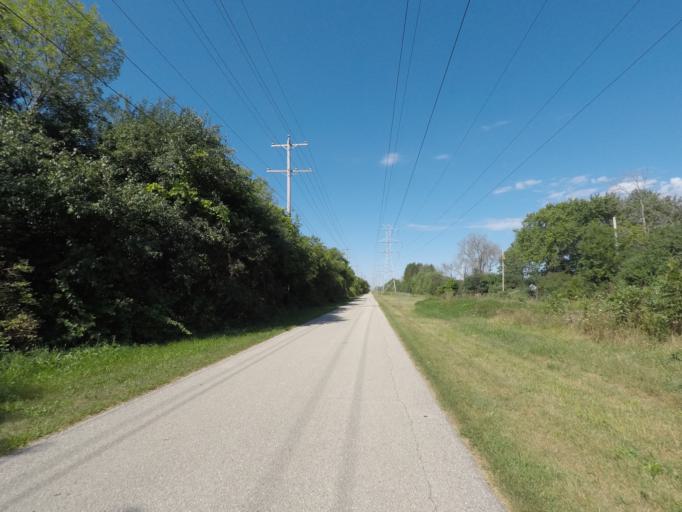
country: US
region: Wisconsin
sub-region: Waukesha County
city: New Berlin
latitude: 43.0101
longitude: -88.1349
